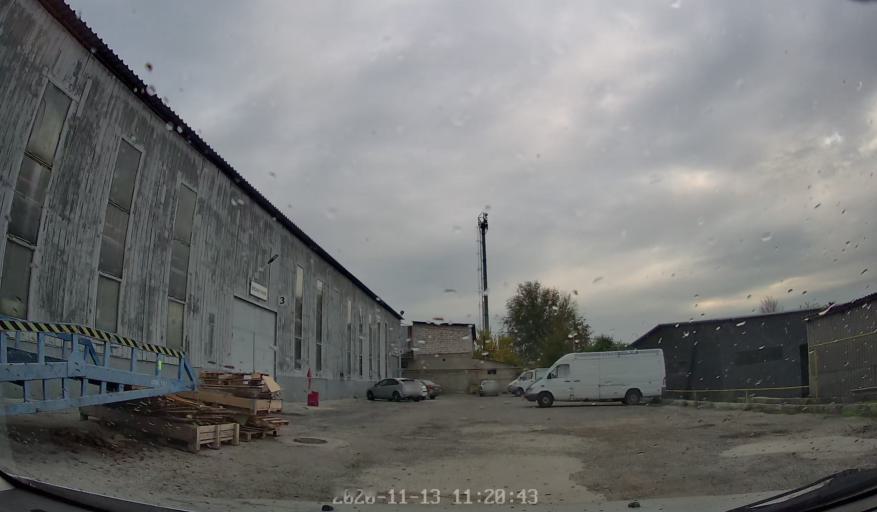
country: MD
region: Chisinau
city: Chisinau
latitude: 46.9862
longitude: 28.9159
